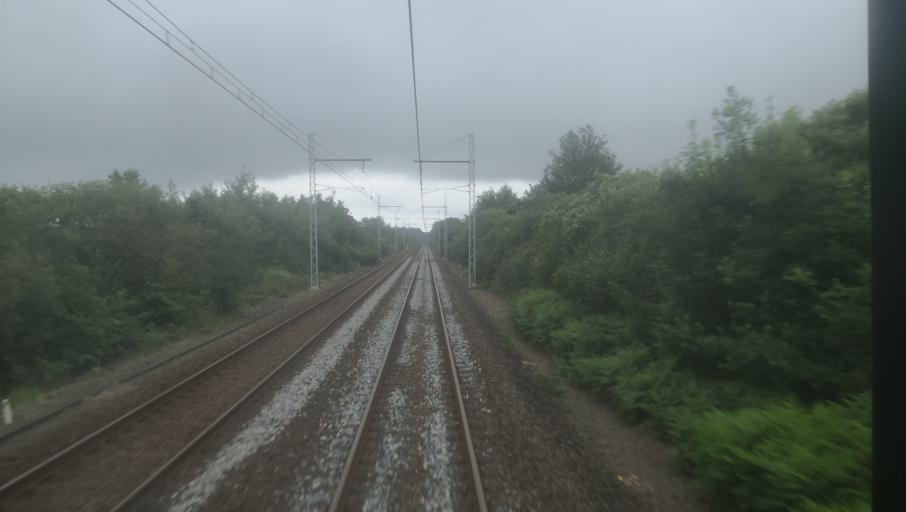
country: FR
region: Centre
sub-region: Departement de l'Indre
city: Luant
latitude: 46.7052
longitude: 1.5701
